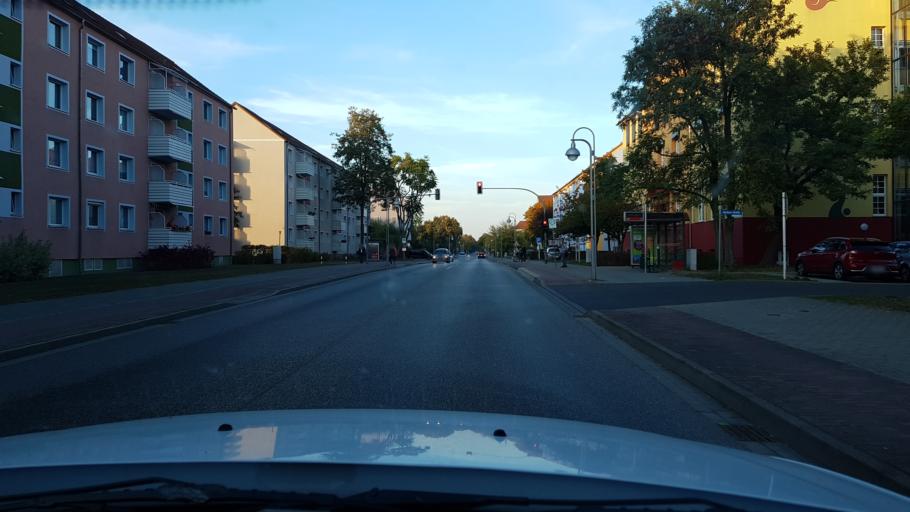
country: DE
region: Brandenburg
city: Schwedt (Oder)
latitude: 53.0589
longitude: 14.2942
